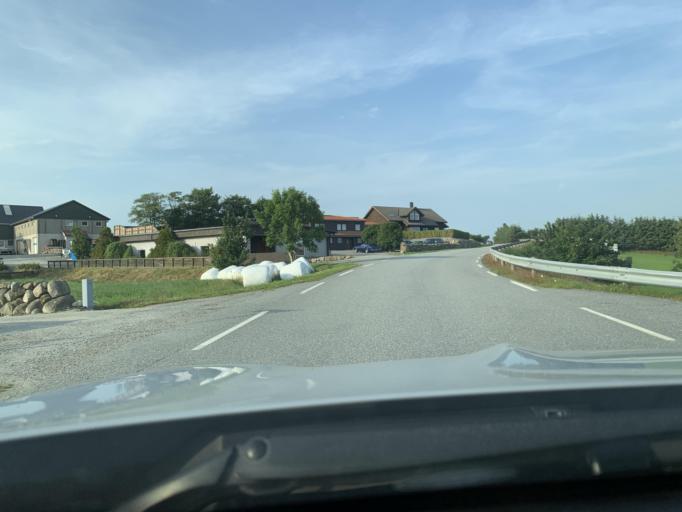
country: NO
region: Rogaland
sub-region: Time
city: Bryne
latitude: 58.7316
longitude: 5.5908
